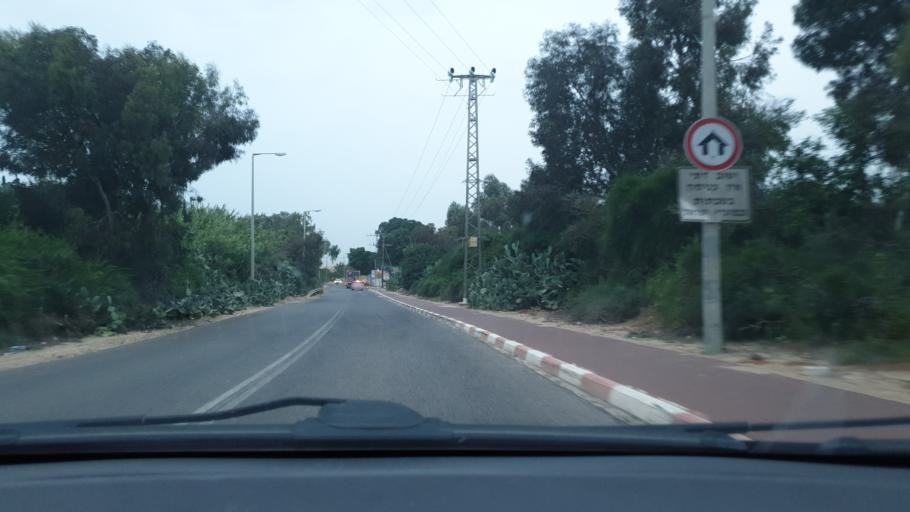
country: IL
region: Central District
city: Kefar Habad
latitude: 31.9849
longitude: 34.8426
